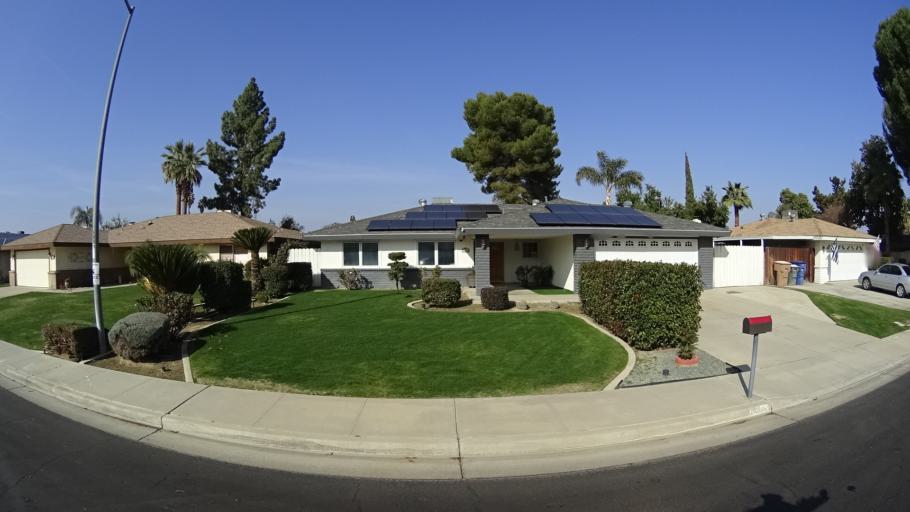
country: US
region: California
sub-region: Kern County
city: Greenacres
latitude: 35.3296
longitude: -119.0699
